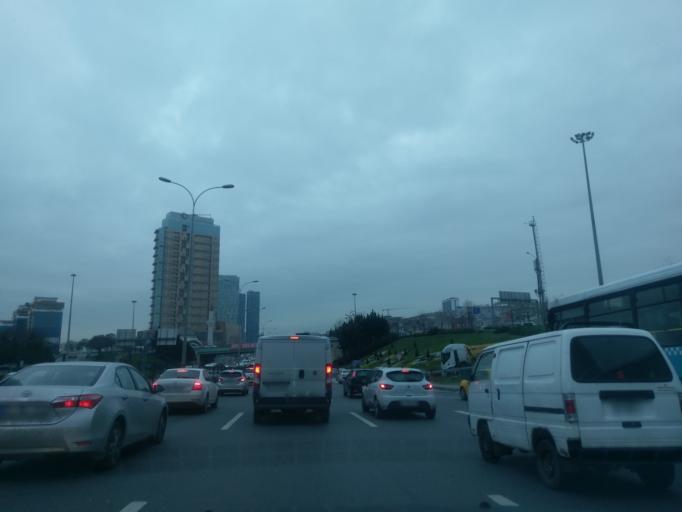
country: TR
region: Istanbul
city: Maltepe
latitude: 40.9184
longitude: 29.1734
